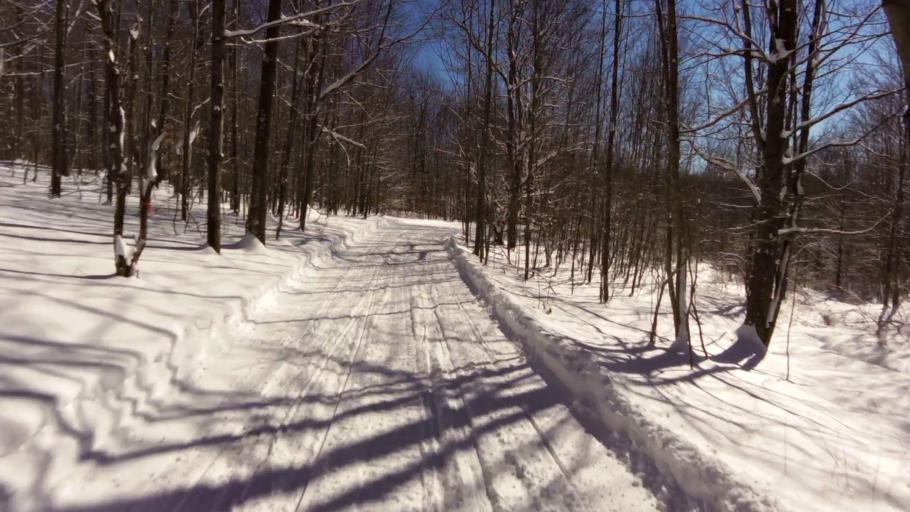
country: US
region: New York
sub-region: Chautauqua County
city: Mayville
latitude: 42.2311
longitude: -79.3922
